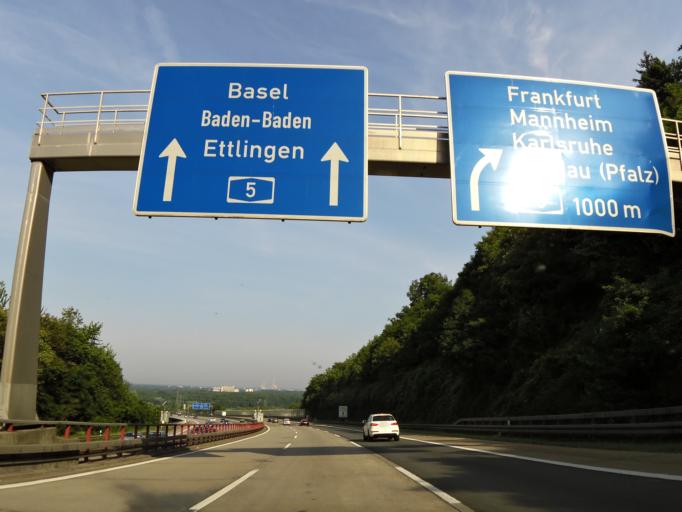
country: DE
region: Baden-Wuerttemberg
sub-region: Karlsruhe Region
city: Ettlingen
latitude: 48.9708
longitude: 8.4585
